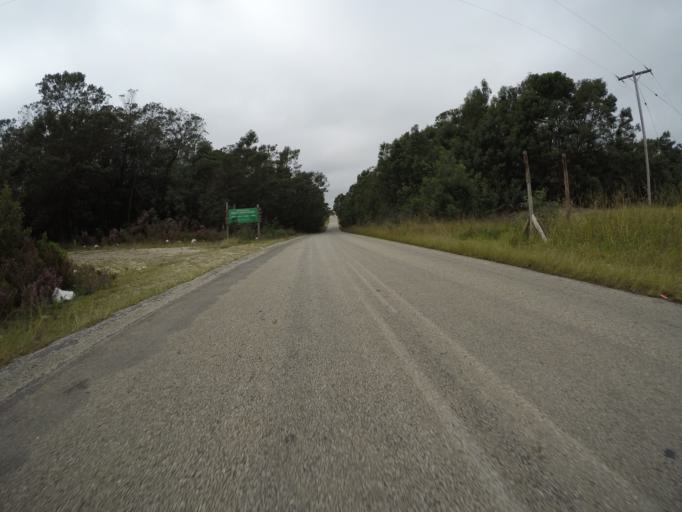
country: ZA
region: Eastern Cape
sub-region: Cacadu District Municipality
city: Kareedouw
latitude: -33.9812
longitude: 24.0482
